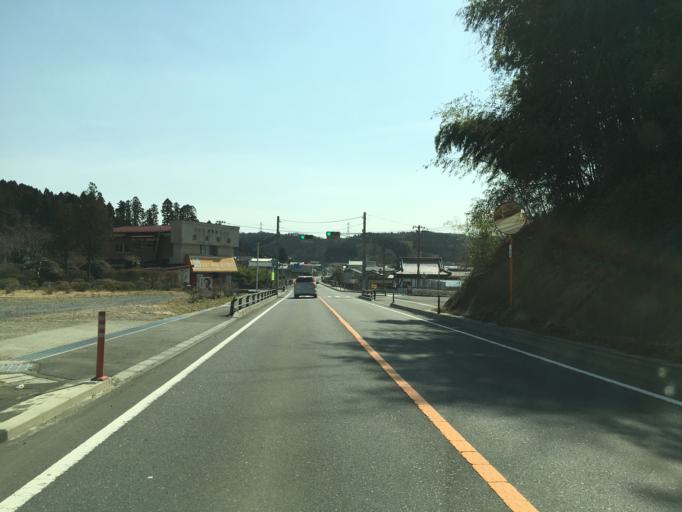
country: JP
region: Fukushima
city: Ishikawa
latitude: 37.1070
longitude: 140.4185
